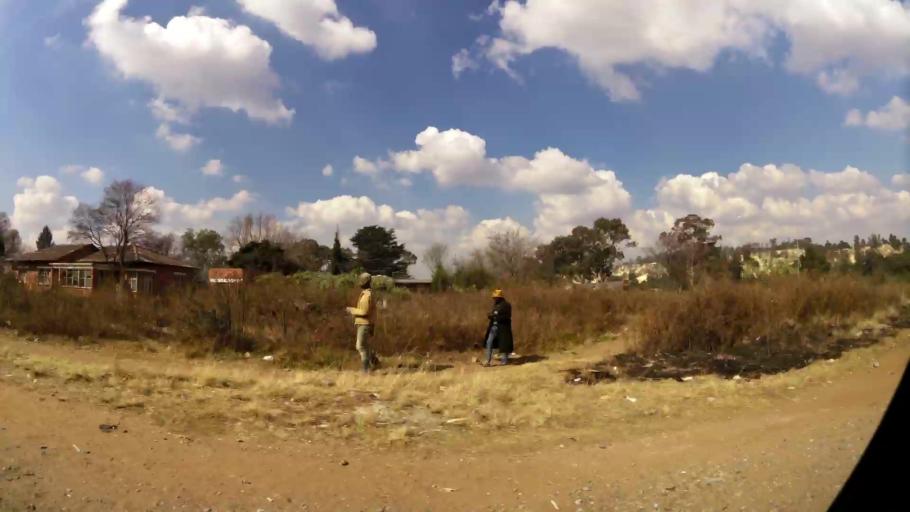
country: ZA
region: Gauteng
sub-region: City of Johannesburg Metropolitan Municipality
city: Roodepoort
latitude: -26.1763
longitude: 27.8720
